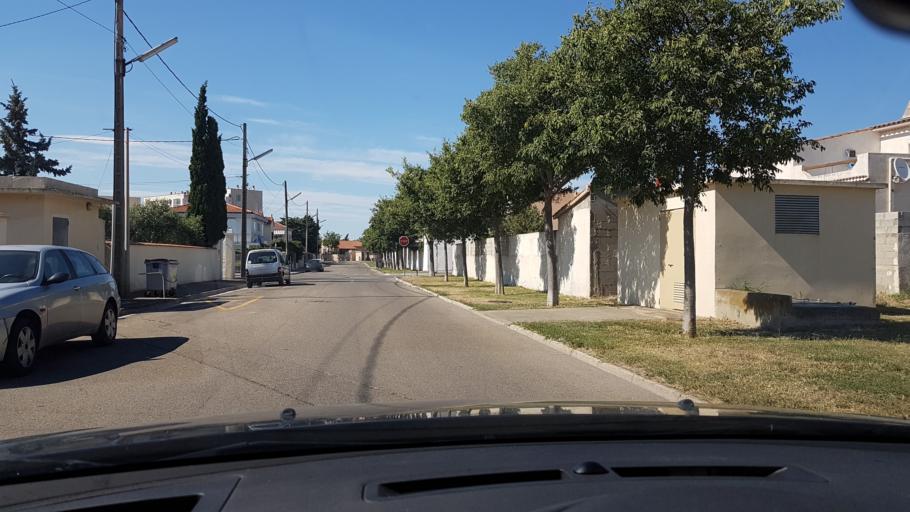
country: FR
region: Provence-Alpes-Cote d'Azur
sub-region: Departement des Bouches-du-Rhone
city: Port-Saint-Louis-du-Rhone
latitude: 43.3886
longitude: 4.8140
